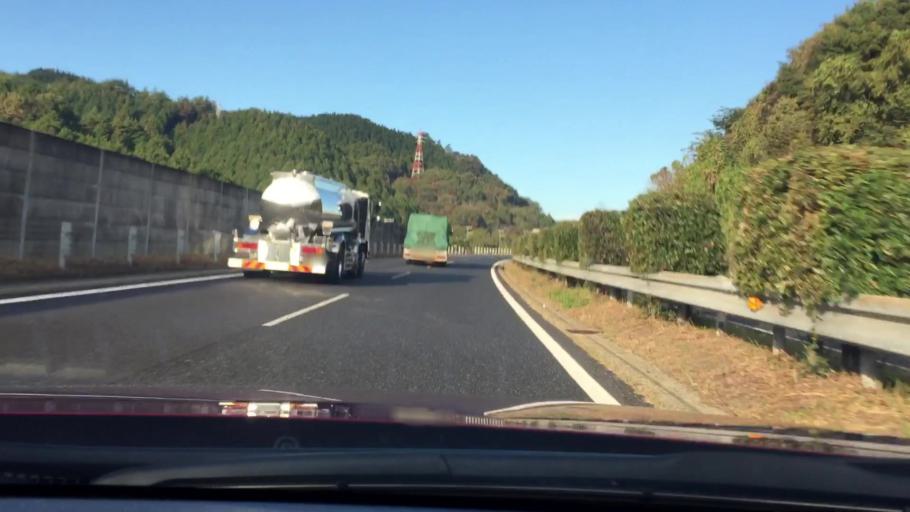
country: JP
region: Hyogo
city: Yamazakicho-nakabirose
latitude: 34.9788
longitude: 134.6274
